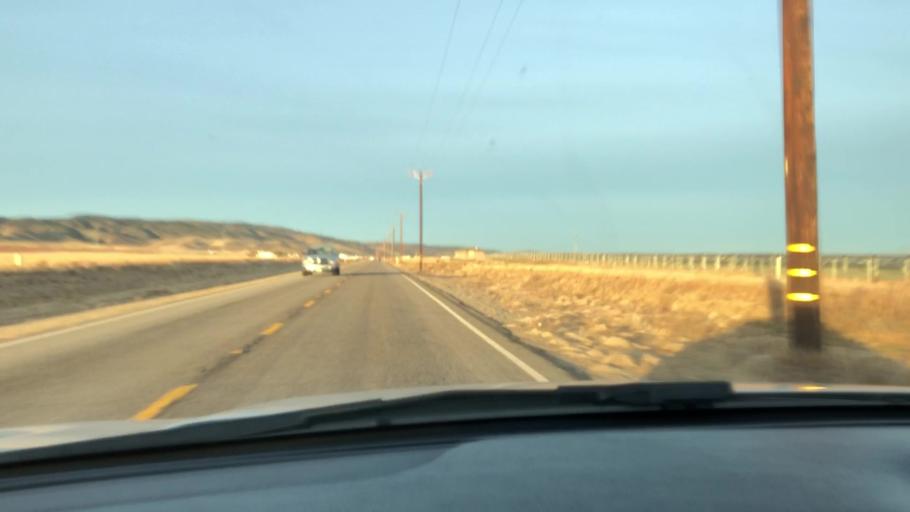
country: US
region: California
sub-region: Los Angeles County
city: Leona Valley
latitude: 34.6747
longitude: -118.3027
